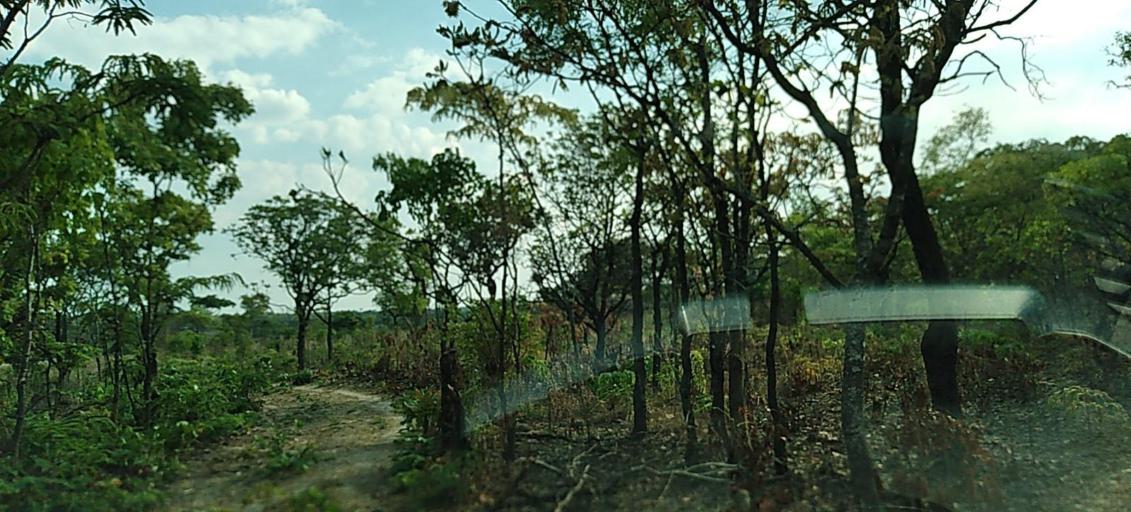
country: ZM
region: Copperbelt
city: Chililabombwe
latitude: -12.3564
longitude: 27.3963
